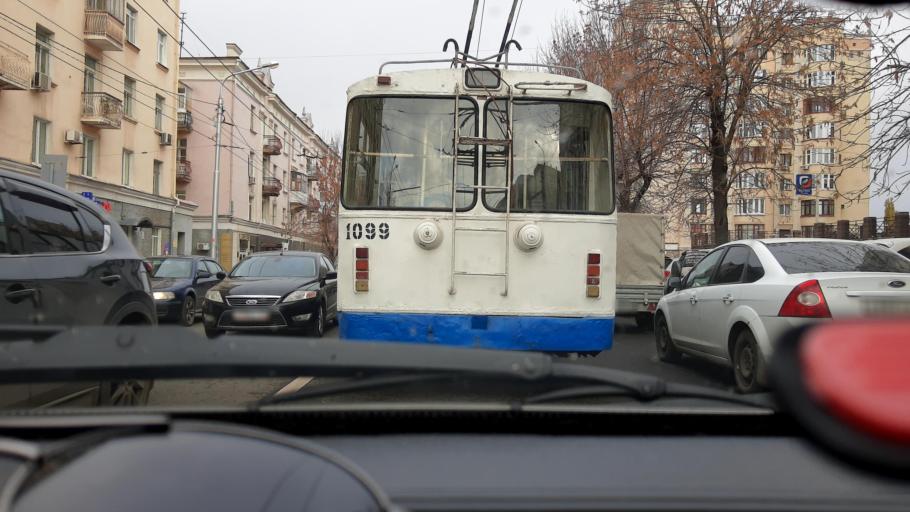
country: RU
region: Bashkortostan
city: Ufa
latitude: 54.7371
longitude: 55.9463
